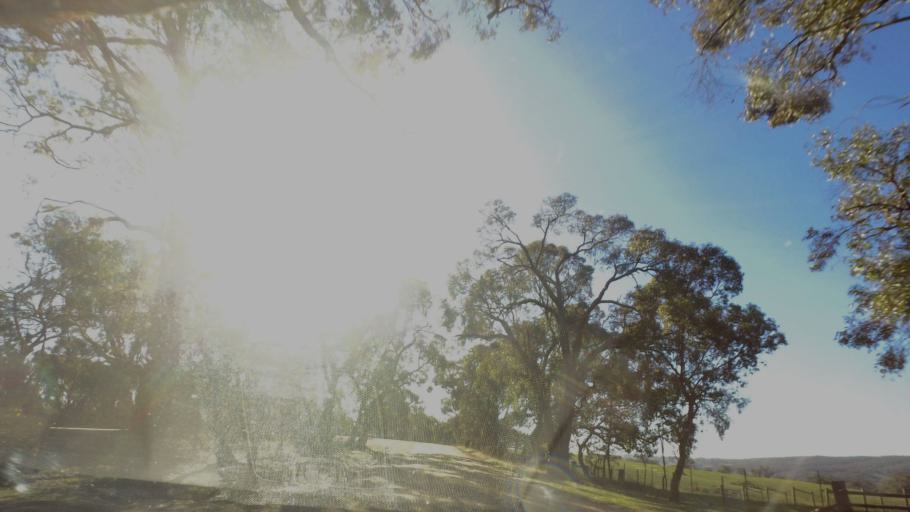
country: AU
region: Victoria
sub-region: Mount Alexander
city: Castlemaine
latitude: -37.1267
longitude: 144.4091
